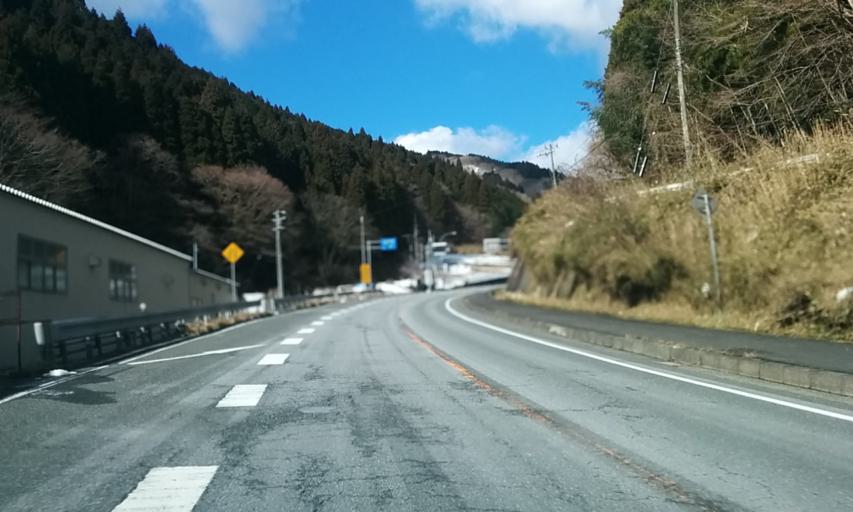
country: JP
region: Kyoto
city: Fukuchiyama
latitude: 35.3978
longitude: 135.0396
